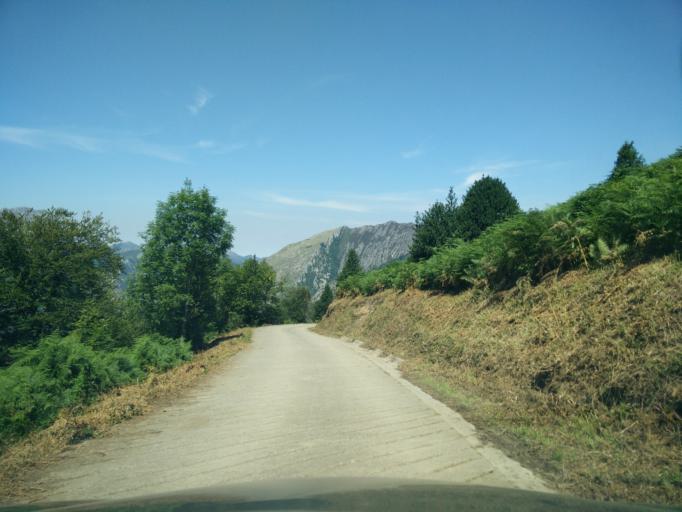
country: ES
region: Asturias
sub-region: Province of Asturias
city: Amieva
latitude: 43.1872
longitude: -5.1426
